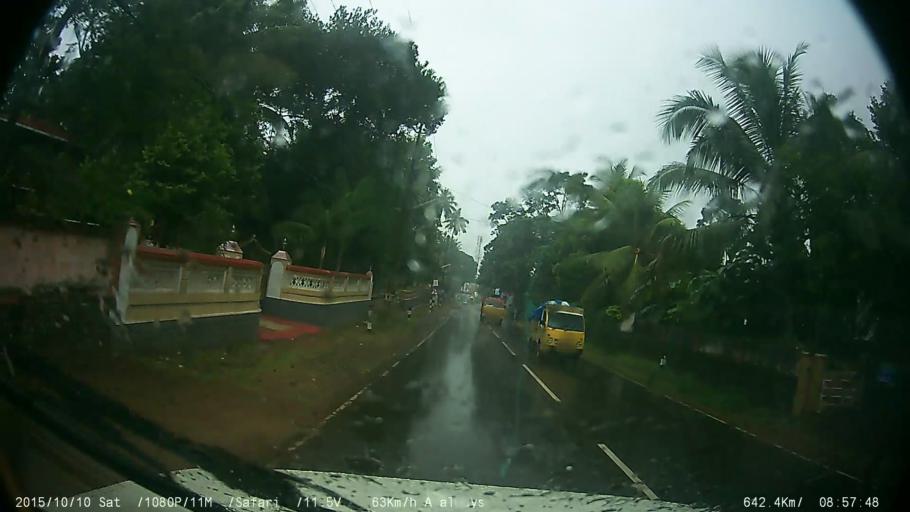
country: IN
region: Kerala
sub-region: Kottayam
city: Palackattumala
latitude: 9.6877
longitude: 76.5559
